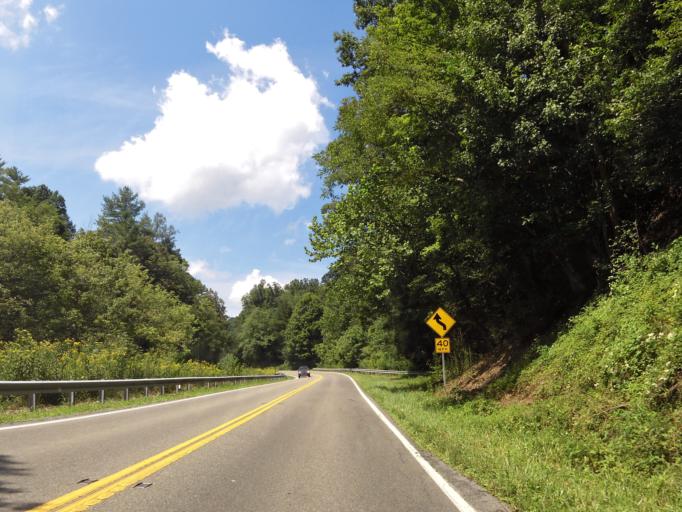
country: US
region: Virginia
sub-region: Washington County
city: Abingdon
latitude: 36.6748
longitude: -81.9726
